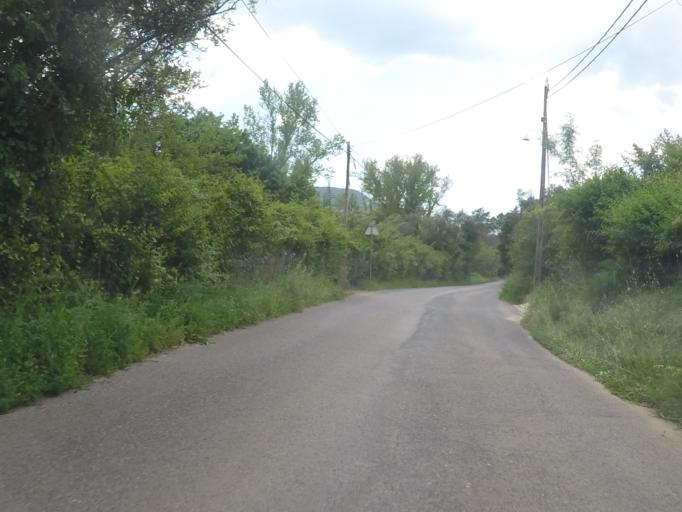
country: PT
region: Setubal
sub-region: Palmela
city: Quinta do Anjo
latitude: 38.5056
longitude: -8.9816
